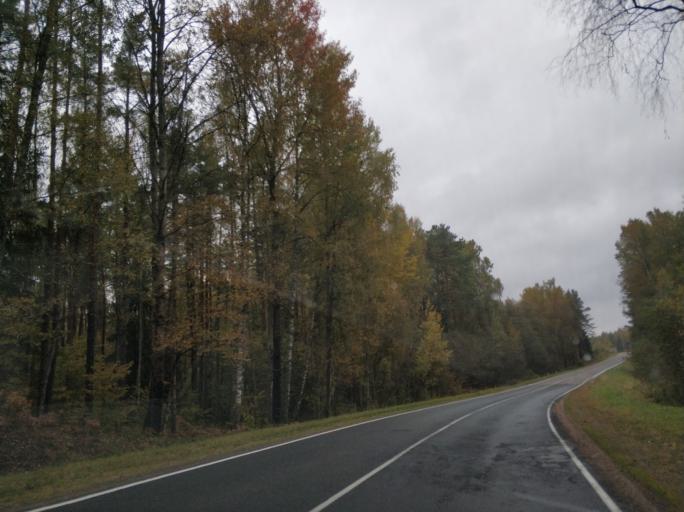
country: RU
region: Pskov
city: Opochka
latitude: 56.5053
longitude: 28.6618
